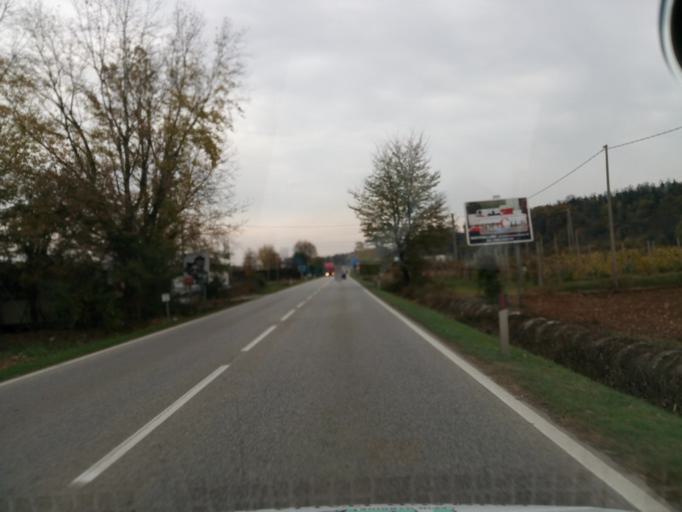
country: IT
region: Veneto
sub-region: Provincia di Treviso
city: Montebelluna
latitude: 45.7889
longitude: 12.0457
